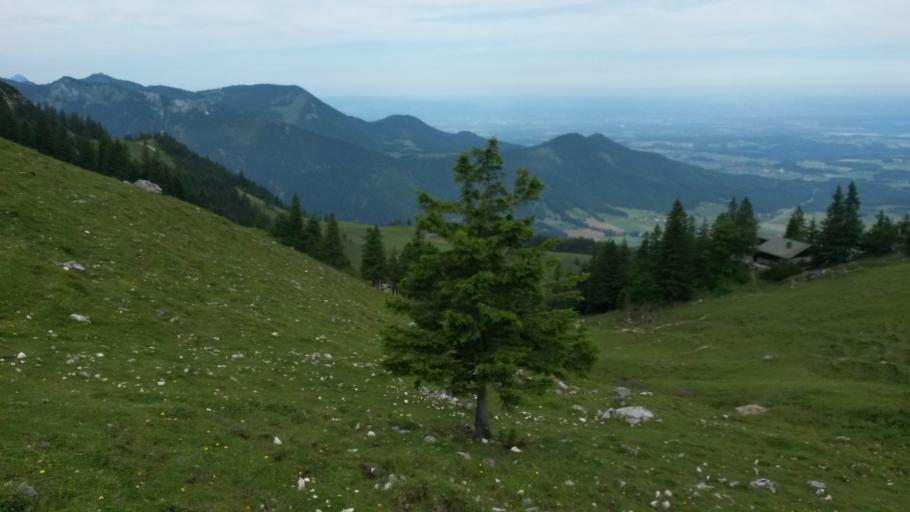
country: DE
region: Bavaria
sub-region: Upper Bavaria
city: Aschau im Chiemgau
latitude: 47.7582
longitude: 12.3642
